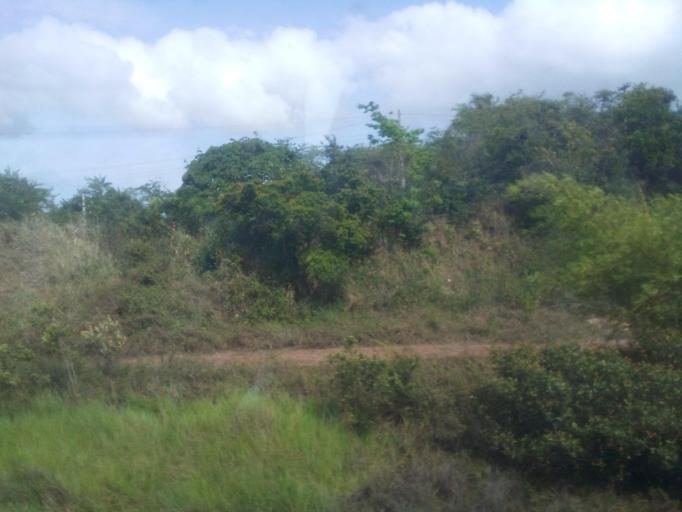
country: BR
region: Maranhao
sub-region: Sao Luis
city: Sao Luis
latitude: -2.7367
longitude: -44.3534
